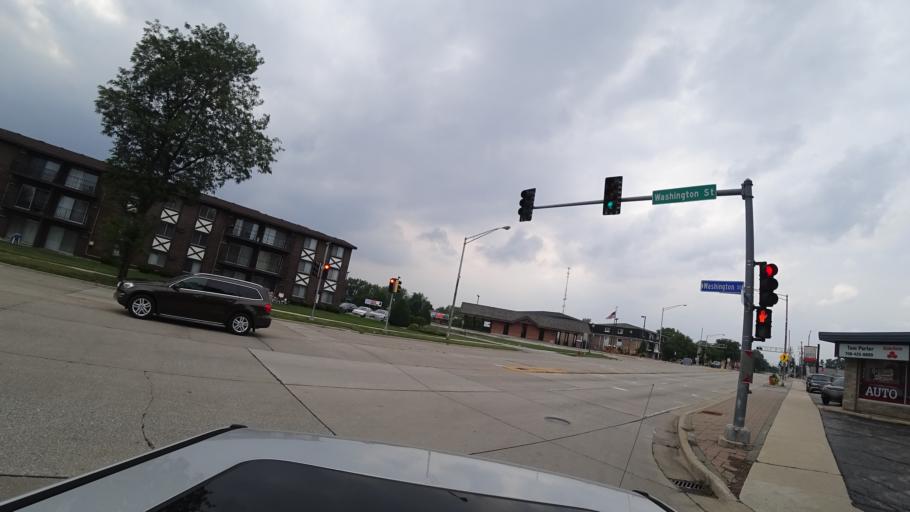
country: US
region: Illinois
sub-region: Cook County
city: Chicago Ridge
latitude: 41.7032
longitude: -87.7792
